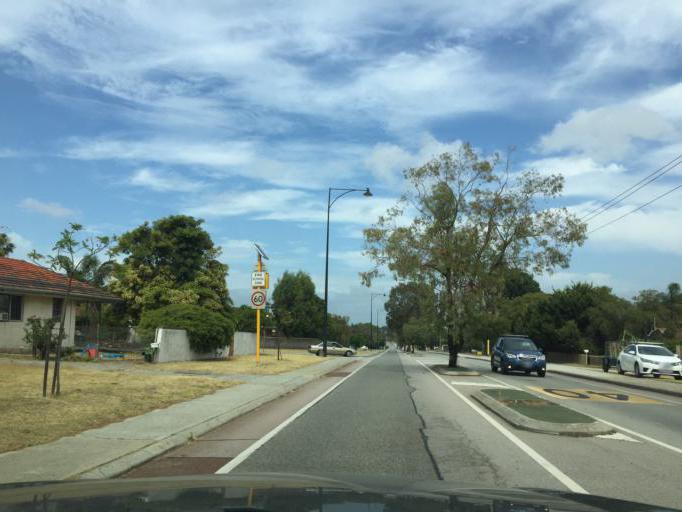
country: AU
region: Western Australia
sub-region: Melville
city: Kardinya
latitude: -32.0747
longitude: 115.8105
